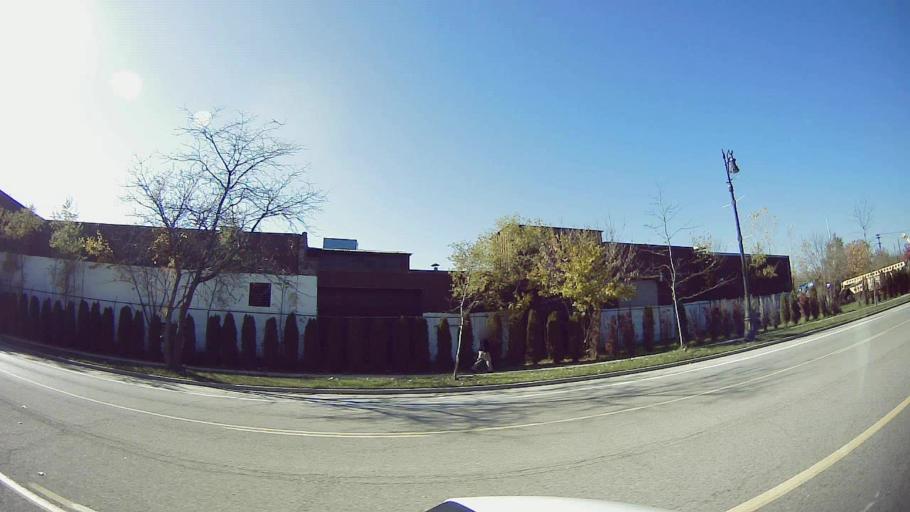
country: US
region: Michigan
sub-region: Wayne County
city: Highland Park
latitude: 42.3610
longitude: -83.0836
